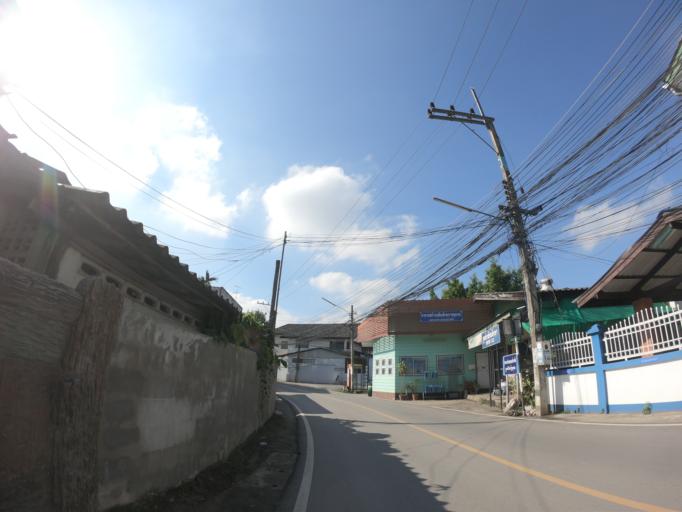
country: TH
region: Chiang Mai
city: Chiang Mai
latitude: 18.7857
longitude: 99.0315
